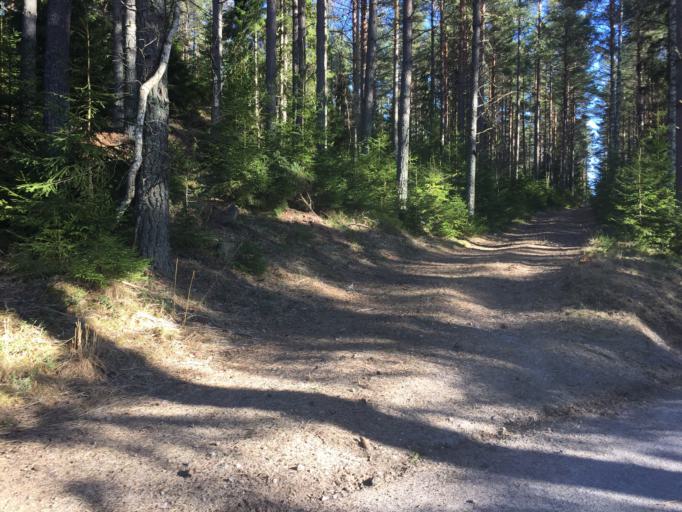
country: SE
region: Soedermanland
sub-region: Vingakers Kommun
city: Vingaker
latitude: 58.9575
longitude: 15.6627
